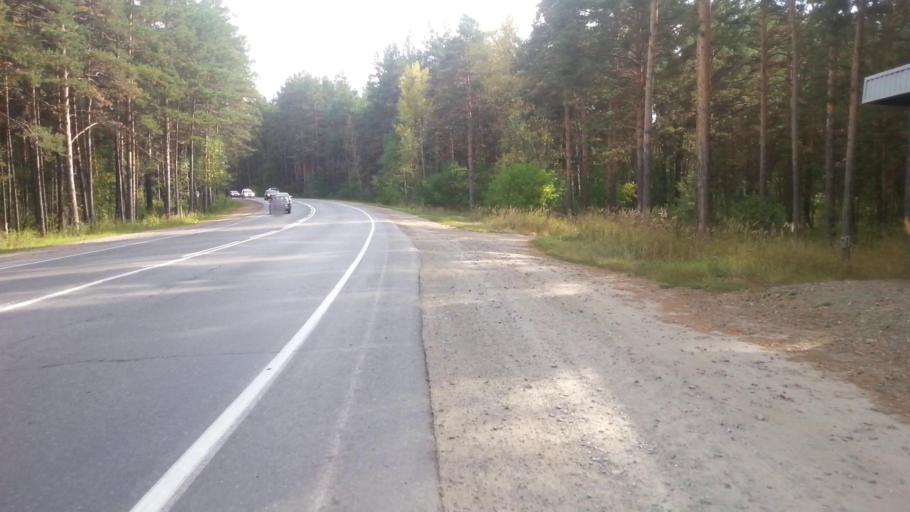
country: RU
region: Altai Krai
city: Yuzhnyy
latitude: 53.2991
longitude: 83.7028
